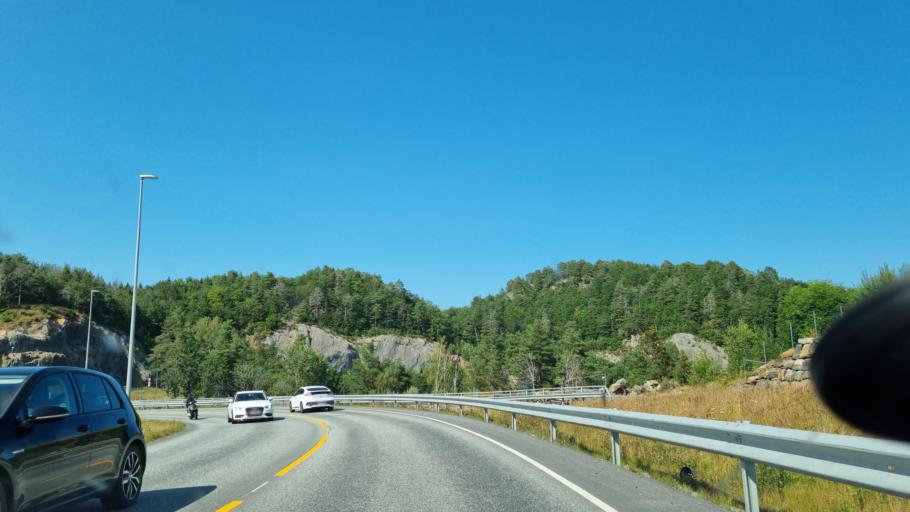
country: NO
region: Aust-Agder
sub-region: Arendal
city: Arendal
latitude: 58.4760
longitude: 8.8193
